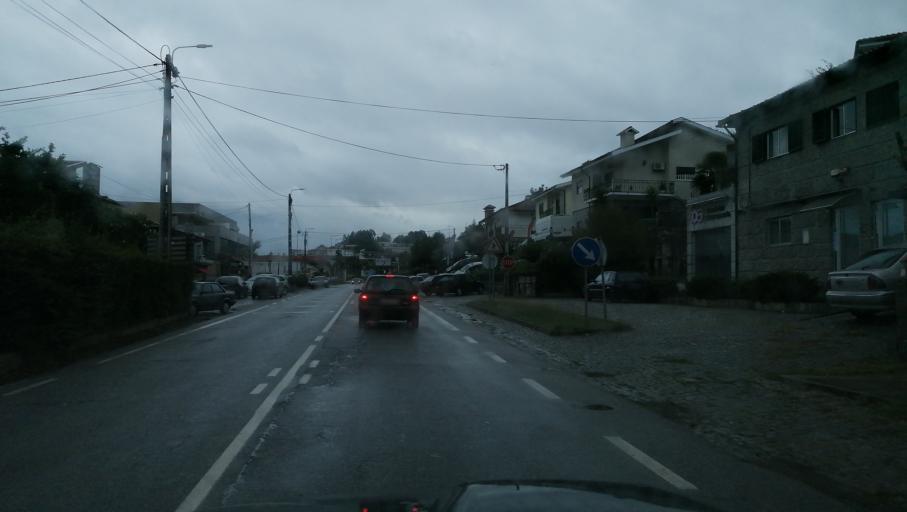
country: PT
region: Braga
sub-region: Guimaraes
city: Moreira de Conegos
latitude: 41.4032
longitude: -8.3231
